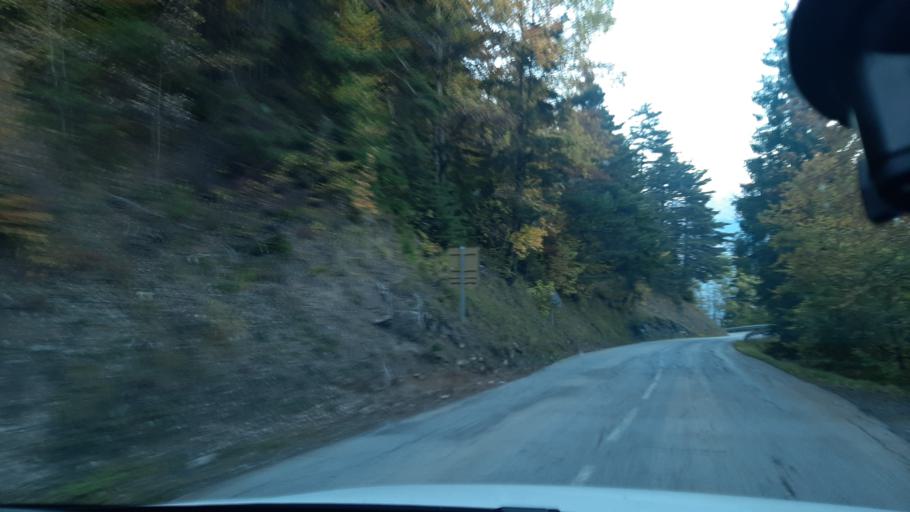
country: FR
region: Rhone-Alpes
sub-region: Departement de la Savoie
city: Saint-Jean-de-Maurienne
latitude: 45.2250
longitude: 6.3038
